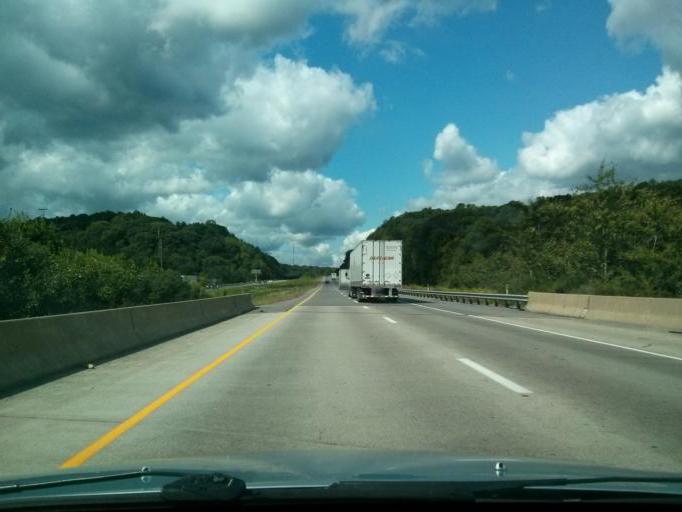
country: US
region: Pennsylvania
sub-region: Clearfield County
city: Treasure Lake
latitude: 41.1220
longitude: -78.6169
